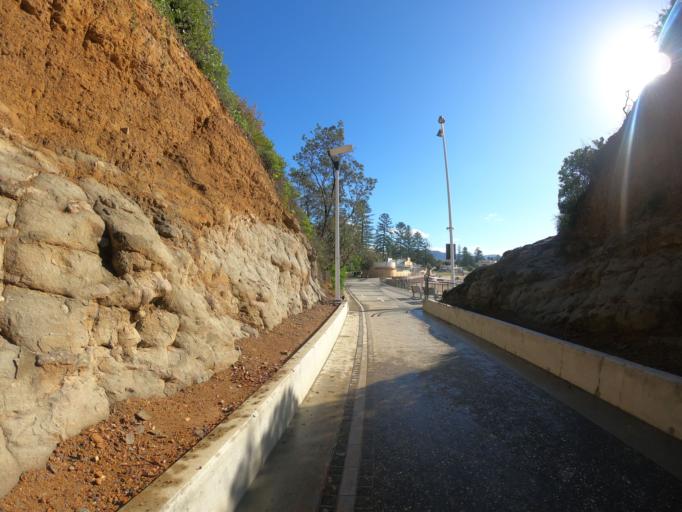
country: AU
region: New South Wales
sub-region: Wollongong
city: Wollongong
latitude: -34.4161
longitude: 150.9018
